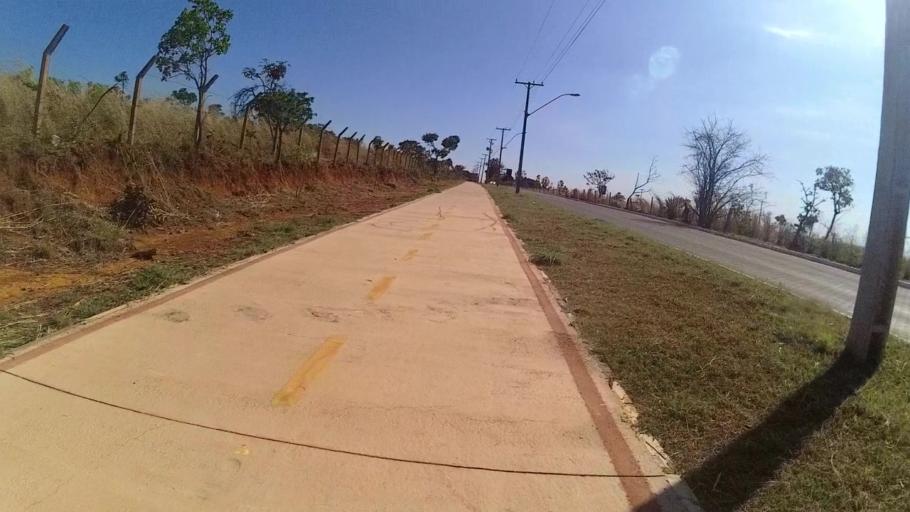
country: BR
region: Federal District
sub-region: Brasilia
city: Brasilia
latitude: -15.6501
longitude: -47.8921
